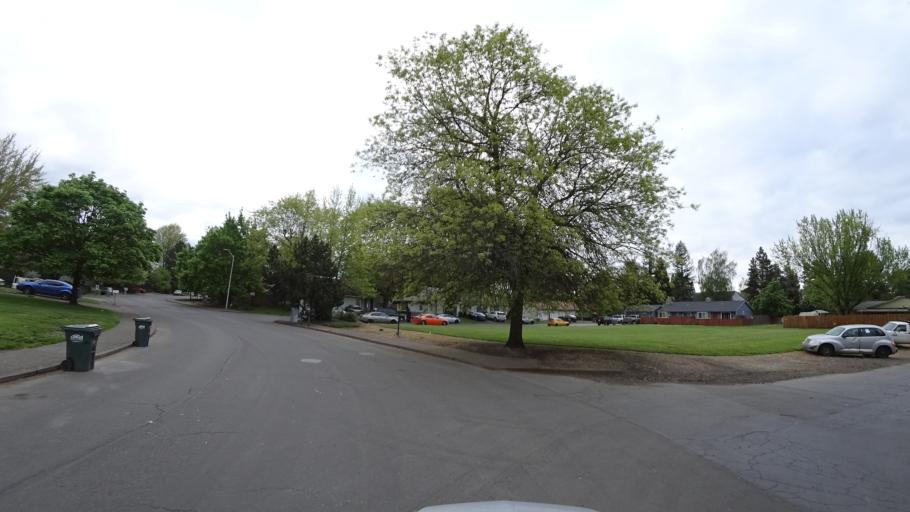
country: US
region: Oregon
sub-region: Washington County
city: Hillsboro
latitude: 45.5343
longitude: -122.9630
